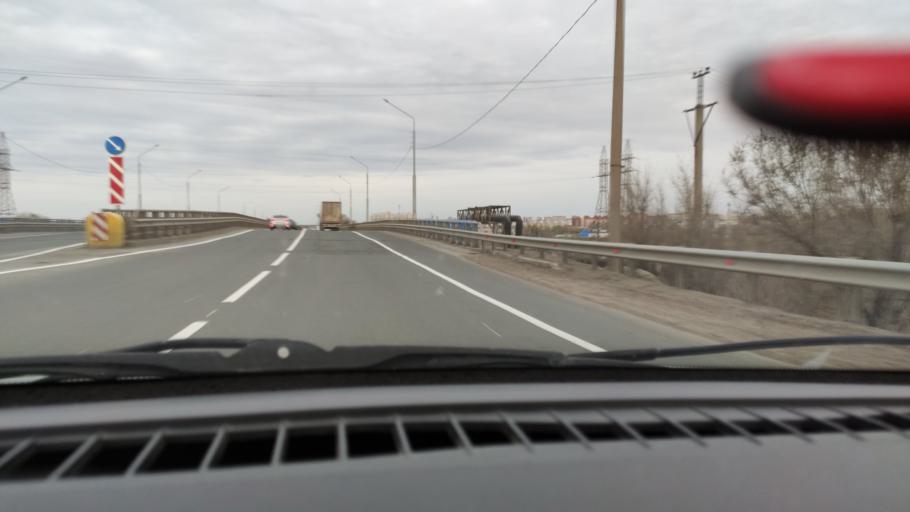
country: RU
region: Orenburg
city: Orenburg
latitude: 51.8530
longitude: 55.1386
